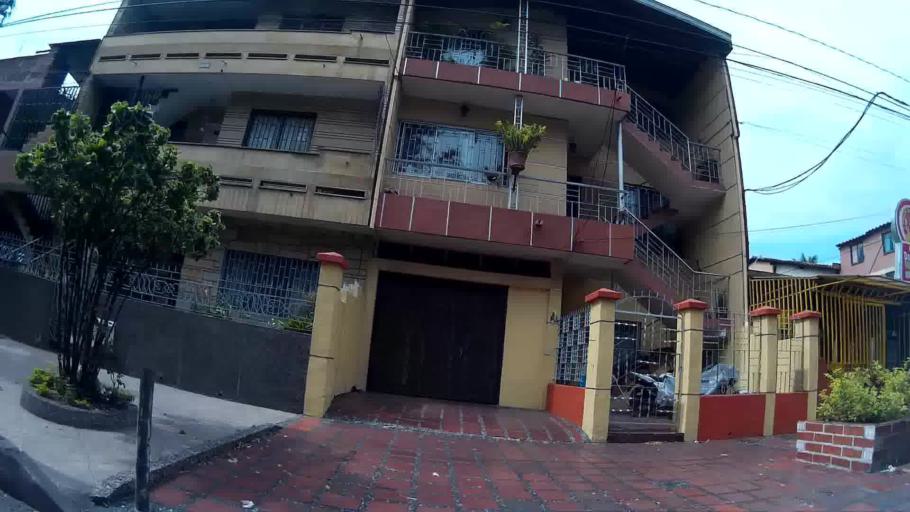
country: CO
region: Antioquia
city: Medellin
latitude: 6.2592
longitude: -75.6056
